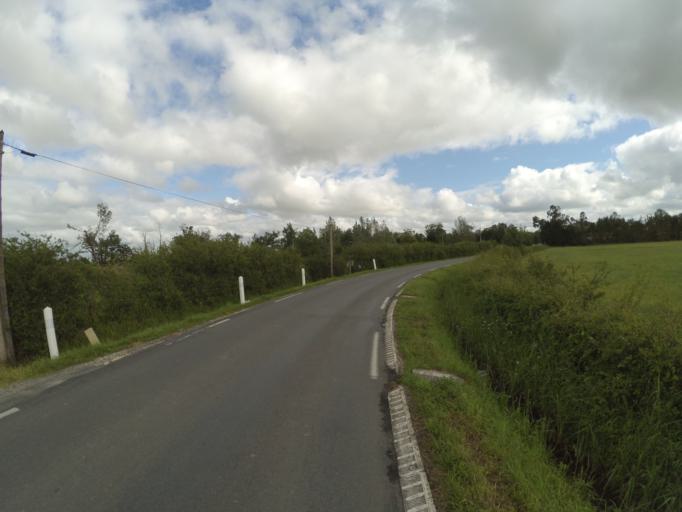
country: FR
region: Aquitaine
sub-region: Departement de la Gironde
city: Ludon-Medoc
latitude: 44.9925
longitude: -0.5851
